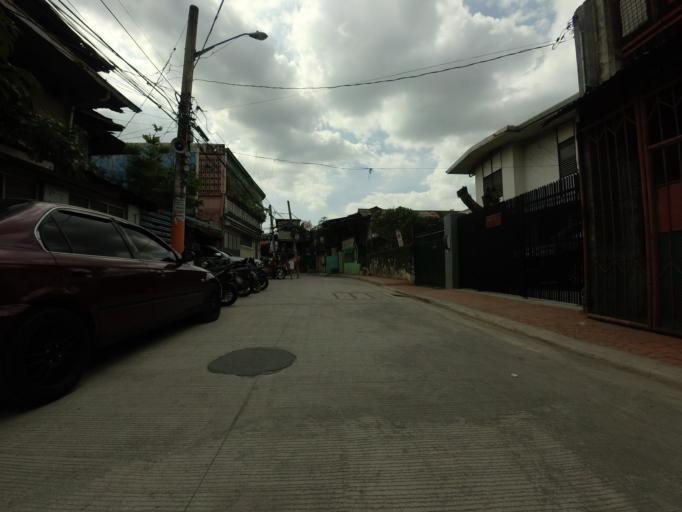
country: PH
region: Metro Manila
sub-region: San Juan
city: San Juan
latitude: 14.5795
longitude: 121.0101
